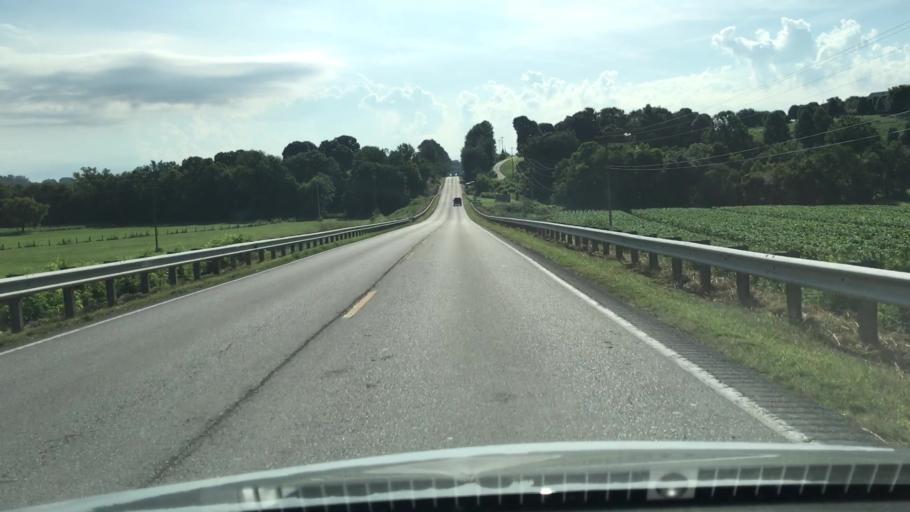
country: US
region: Kentucky
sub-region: Metcalfe County
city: Edmonton
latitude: 36.9886
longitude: -85.6477
